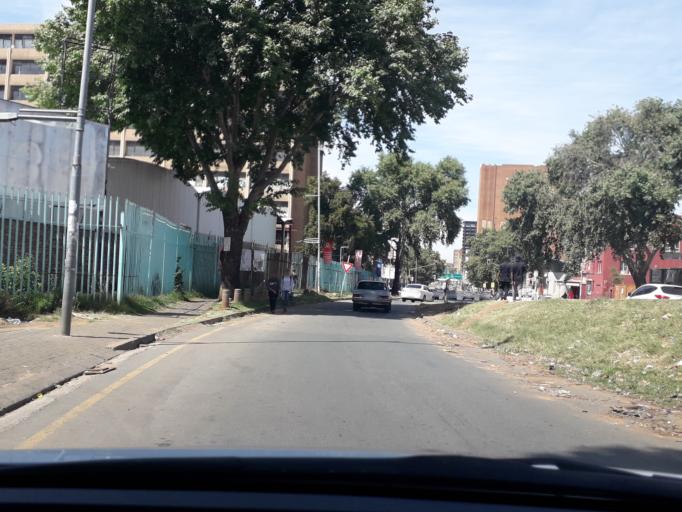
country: ZA
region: Gauteng
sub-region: City of Johannesburg Metropolitan Municipality
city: Johannesburg
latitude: -26.1936
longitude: 28.0591
